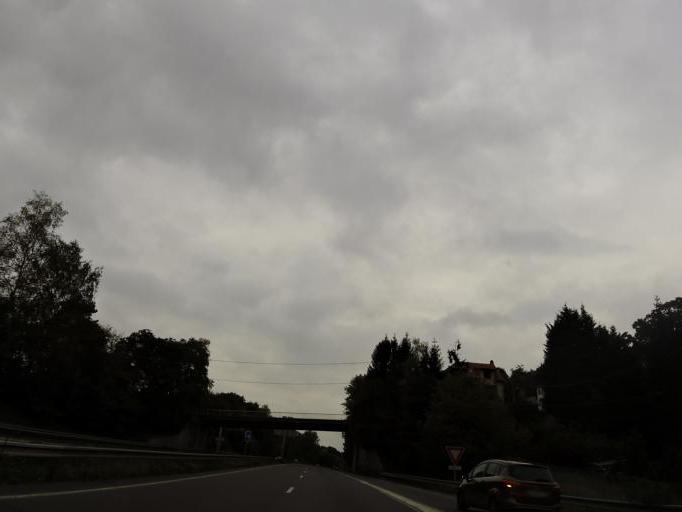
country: FR
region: Lorraine
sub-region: Departement de la Moselle
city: OEting
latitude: 49.1818
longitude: 6.9183
